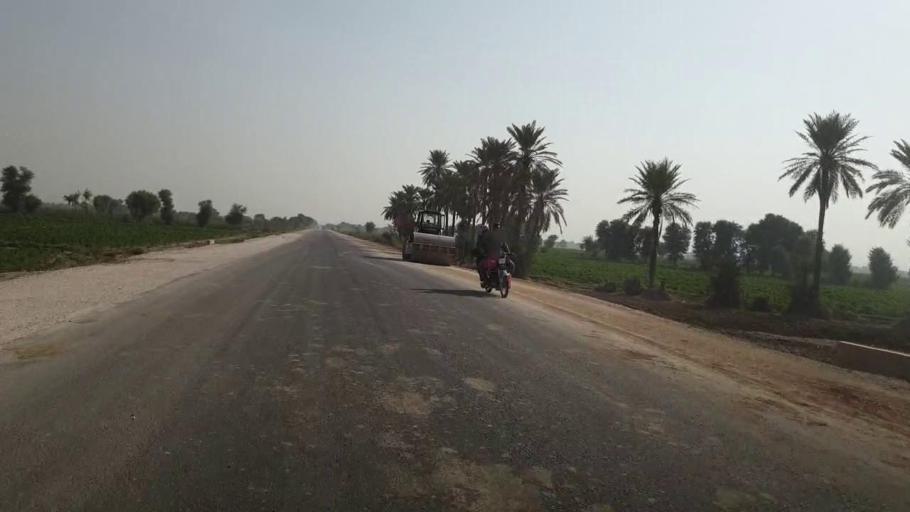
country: PK
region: Sindh
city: Bhan
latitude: 26.5465
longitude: 67.7868
